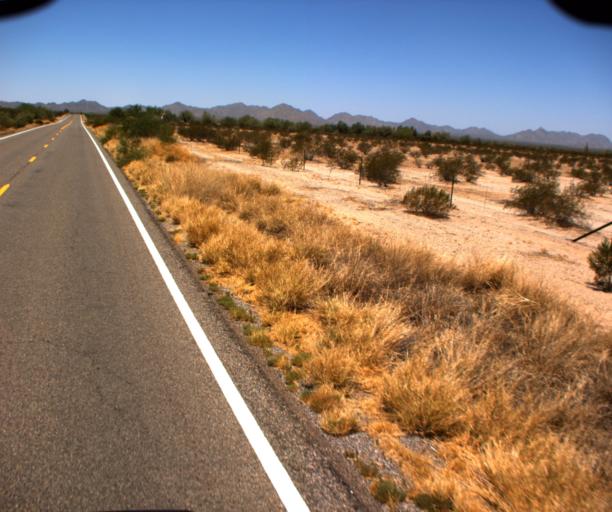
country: US
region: Arizona
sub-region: Pinal County
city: Maricopa
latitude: 33.0374
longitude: -112.3431
